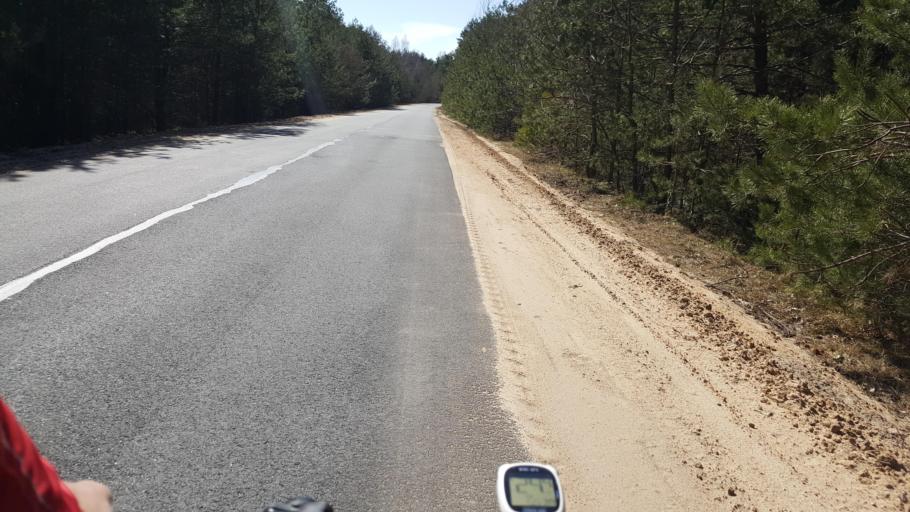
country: BY
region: Brest
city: Charnawchytsy
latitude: 52.2936
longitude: 23.8165
